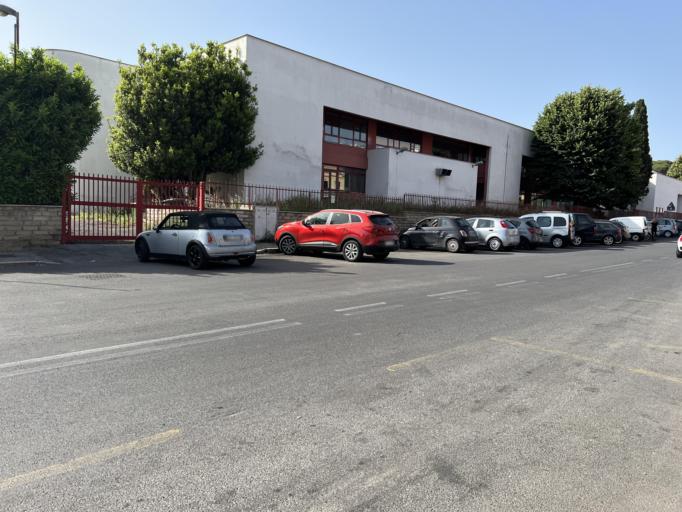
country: VA
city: Vatican City
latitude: 41.8742
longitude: 12.4134
